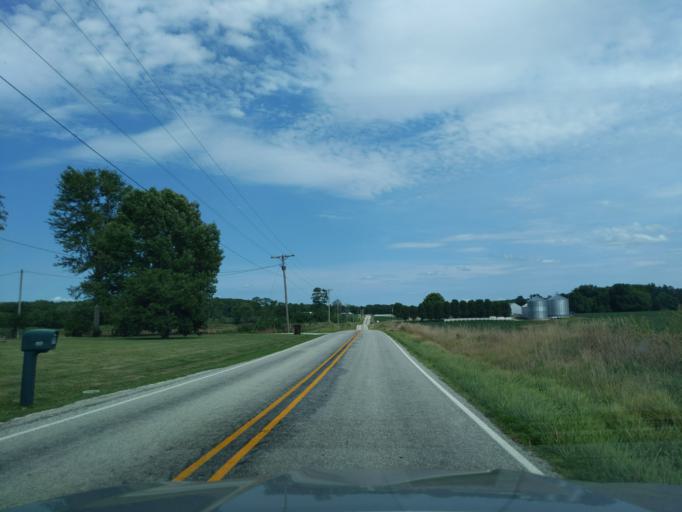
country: US
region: Indiana
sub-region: Ripley County
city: Osgood
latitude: 39.1958
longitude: -85.2356
